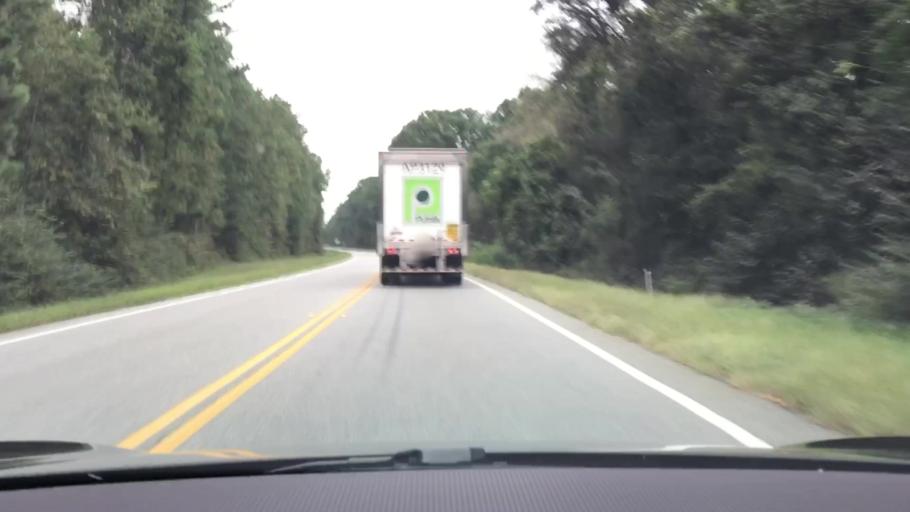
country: US
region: Georgia
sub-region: Greene County
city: Greensboro
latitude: 33.6955
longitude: -83.2779
